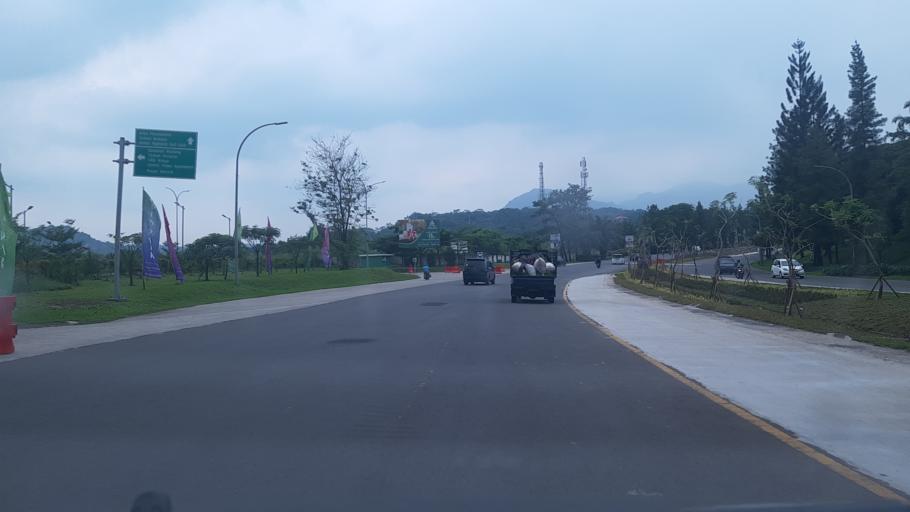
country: ID
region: West Java
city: Bogor
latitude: -6.5681
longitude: 106.8599
